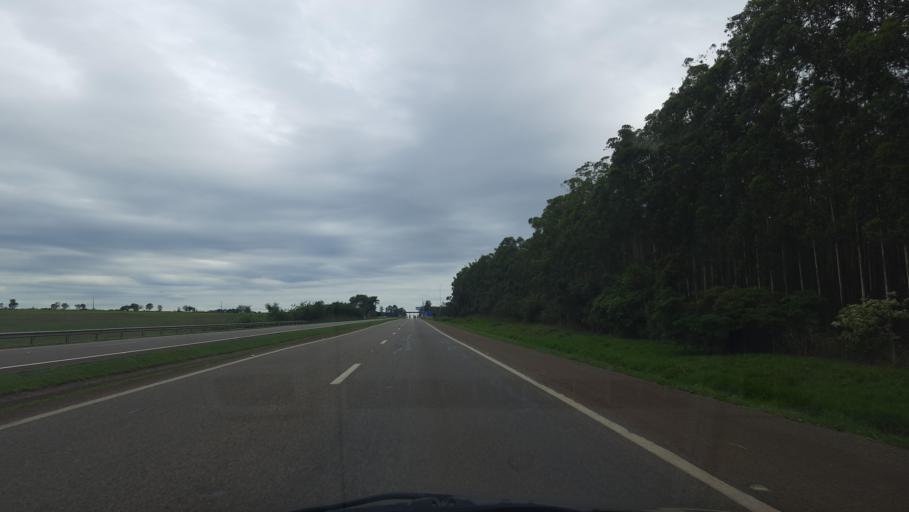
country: BR
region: Sao Paulo
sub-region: Casa Branca
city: Casa Branca
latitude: -21.9111
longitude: -47.0533
